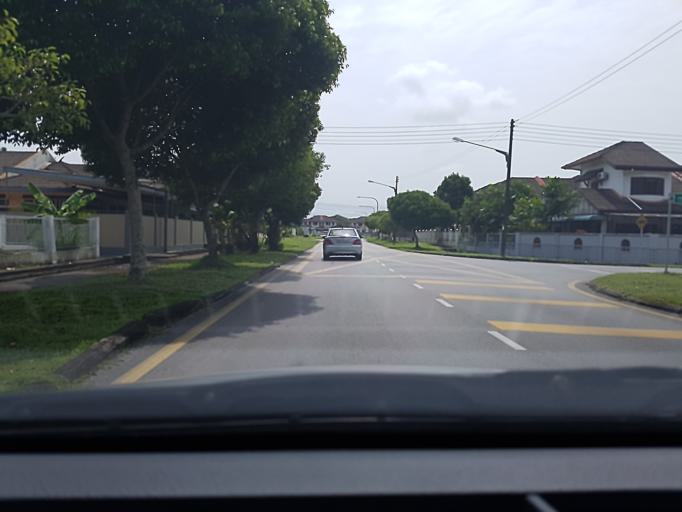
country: MY
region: Sarawak
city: Kuching
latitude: 1.5157
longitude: 110.3626
